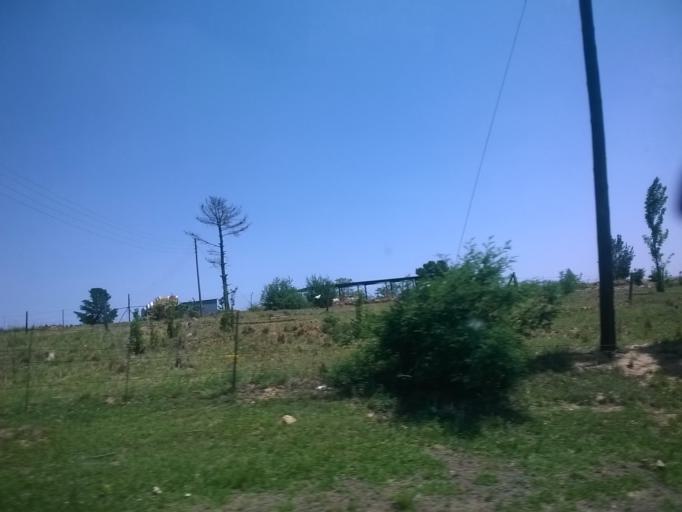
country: LS
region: Berea
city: Teyateyaneng
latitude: -29.1360
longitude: 27.7681
